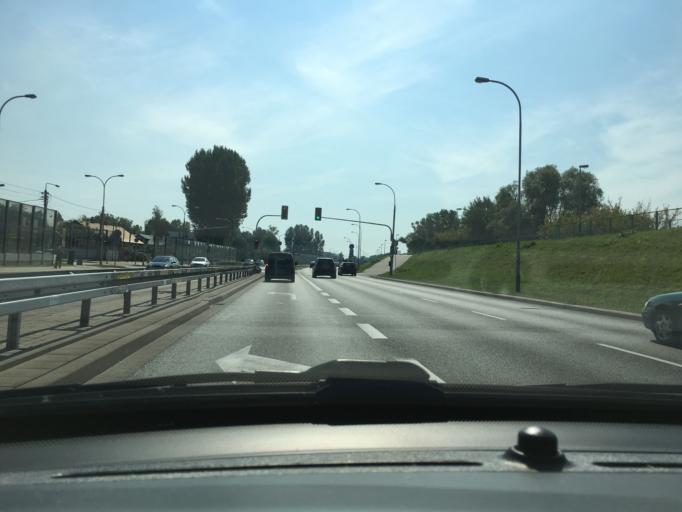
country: PL
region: Masovian Voivodeship
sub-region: Warszawa
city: Wilanow
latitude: 52.1999
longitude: 21.1177
